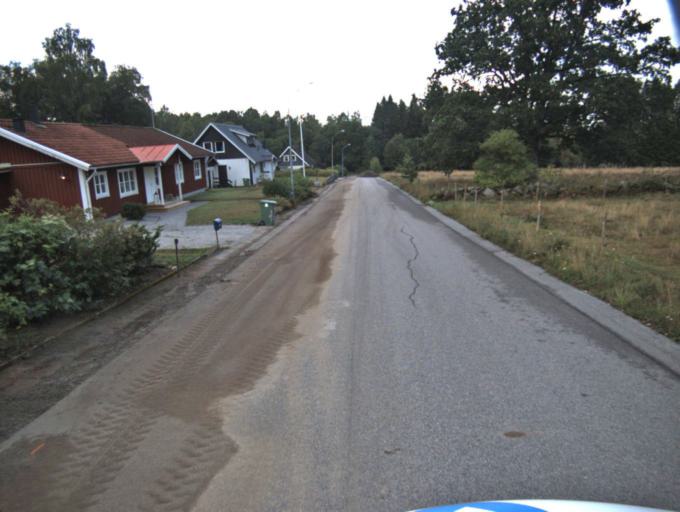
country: SE
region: Vaestra Goetaland
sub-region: Ulricehamns Kommun
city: Ulricehamn
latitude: 57.6778
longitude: 13.4631
